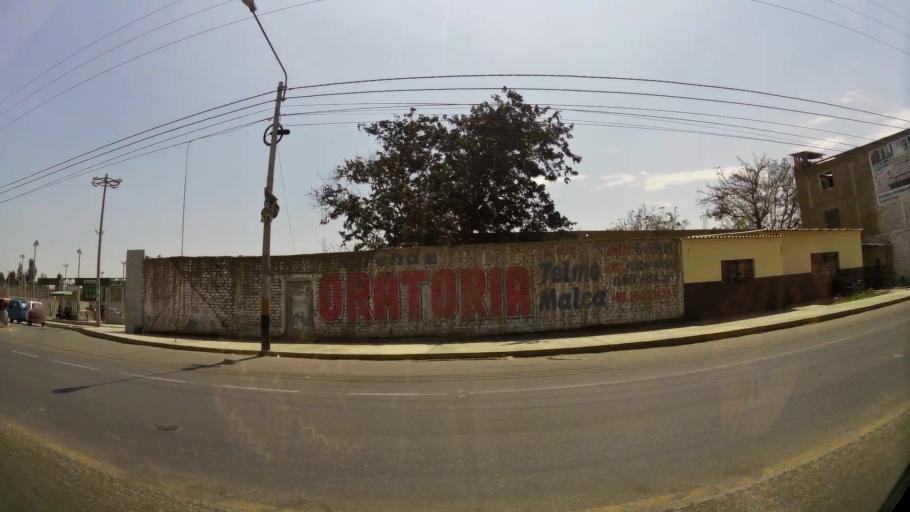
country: PE
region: La Libertad
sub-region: Chepen
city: Chepen
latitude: -7.2218
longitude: -79.4376
